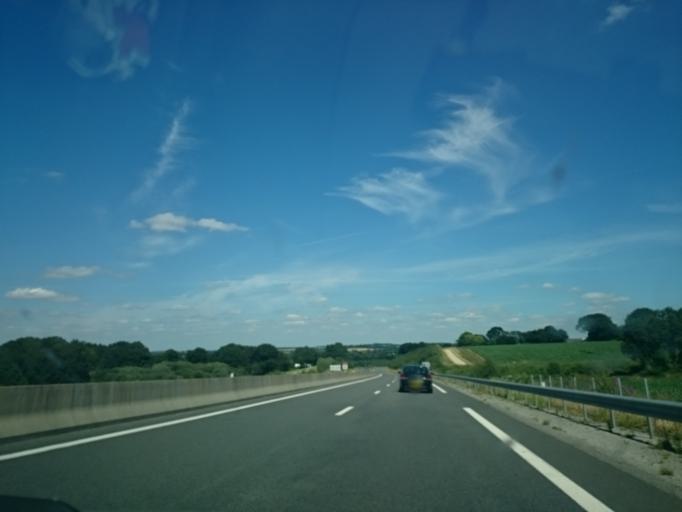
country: FR
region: Brittany
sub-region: Departement des Cotes-d'Armor
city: Gouarec
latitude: 48.2333
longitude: -3.1917
